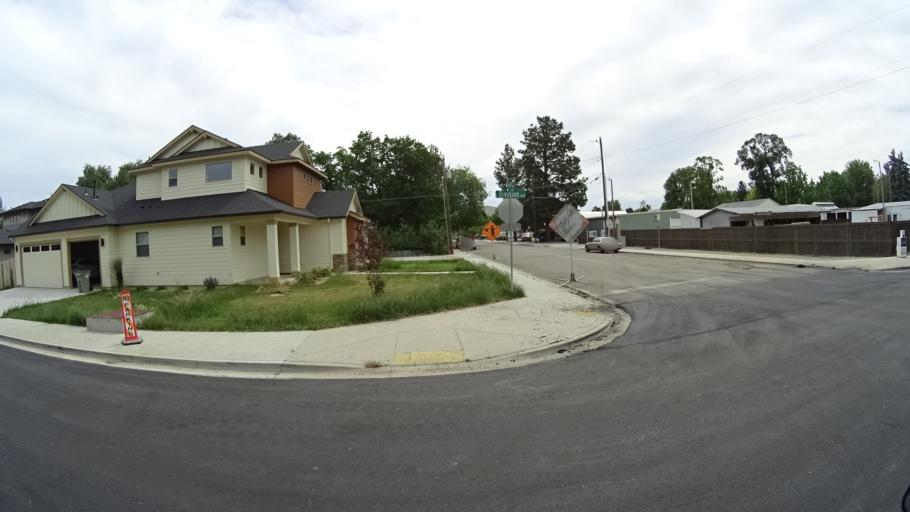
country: US
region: Idaho
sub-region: Ada County
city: Boise
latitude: 43.5947
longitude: -116.1886
